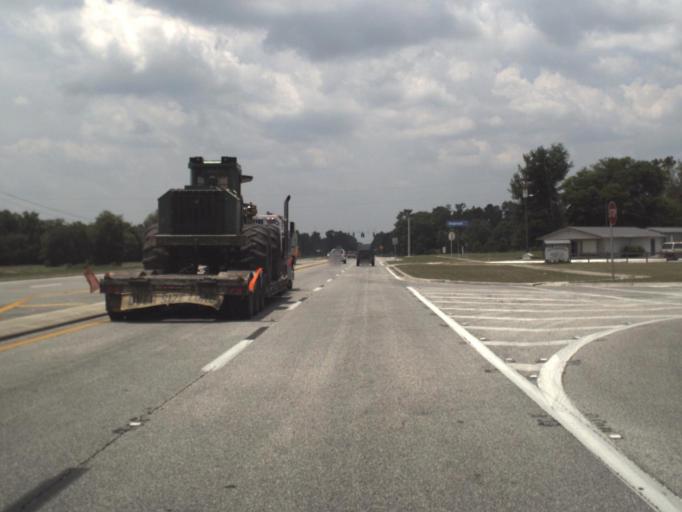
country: US
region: Florida
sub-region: Putnam County
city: Palatka
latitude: 29.6364
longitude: -81.6796
